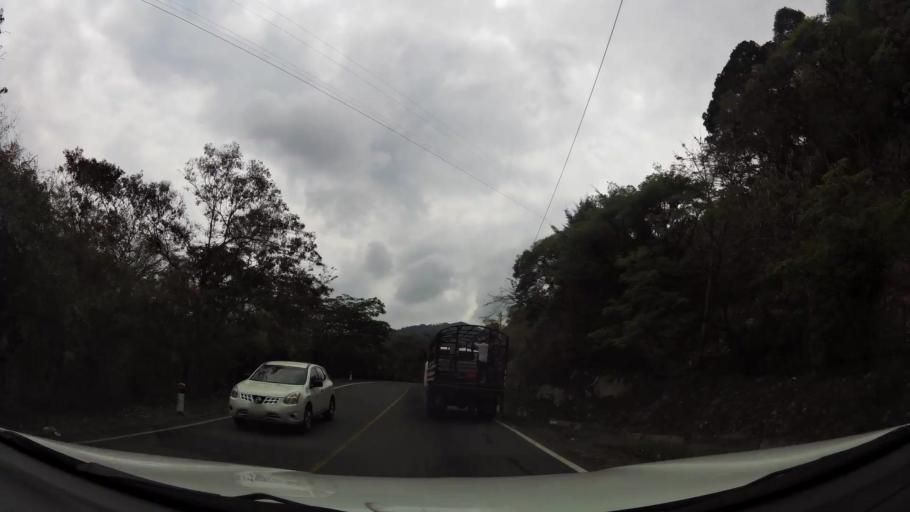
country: NI
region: Matagalpa
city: Matagalpa
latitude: 12.9657
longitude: -85.9191
